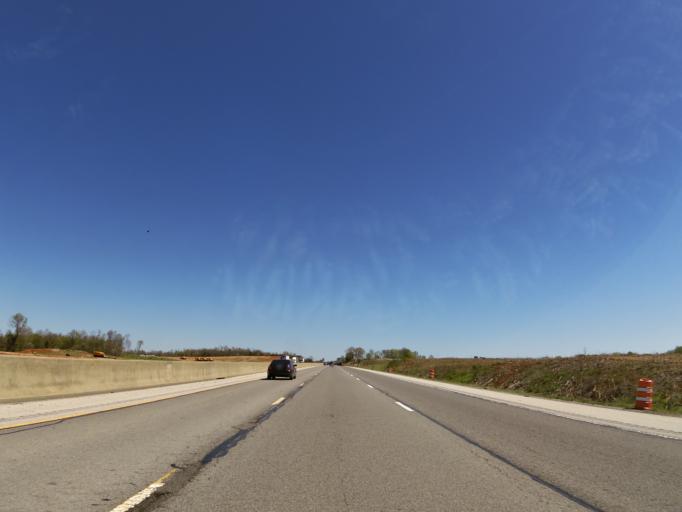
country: US
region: Kentucky
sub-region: Warren County
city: Bowling Green
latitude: 37.0114
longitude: -86.3329
